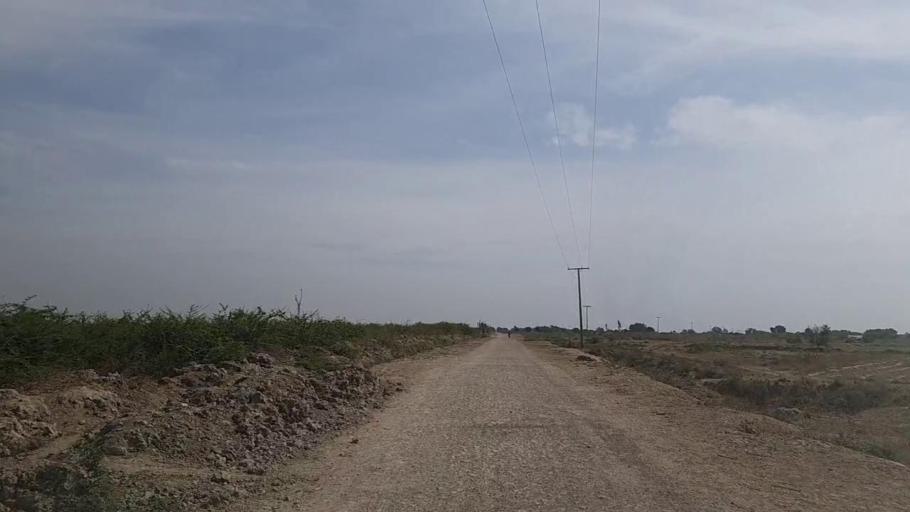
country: PK
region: Sindh
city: Samaro
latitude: 25.2053
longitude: 69.4607
